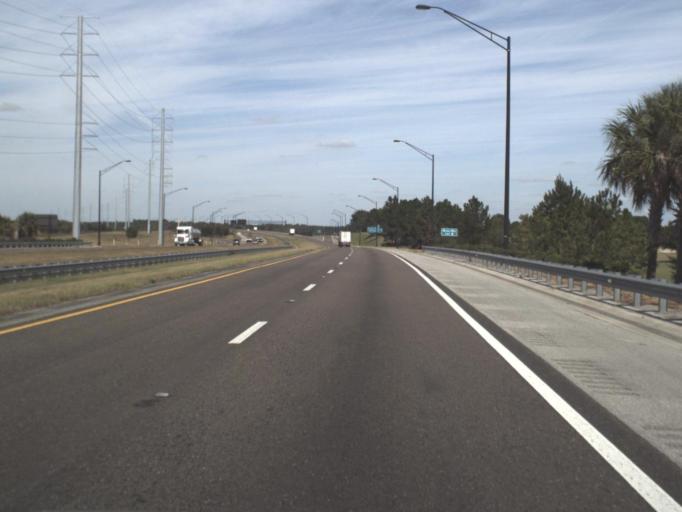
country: US
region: Florida
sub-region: Polk County
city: Citrus Ridge
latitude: 28.3682
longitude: -81.6097
